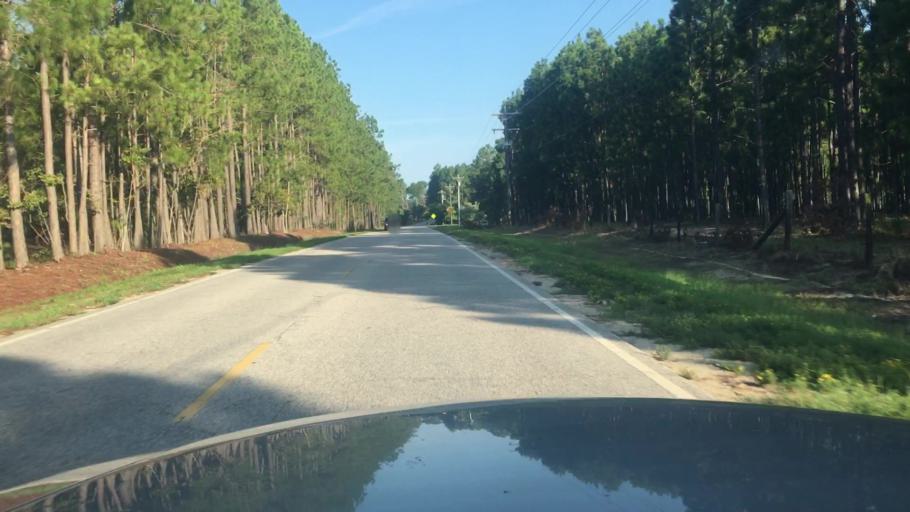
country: US
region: North Carolina
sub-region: Harnett County
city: Walkertown
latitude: 35.2098
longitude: -78.8588
